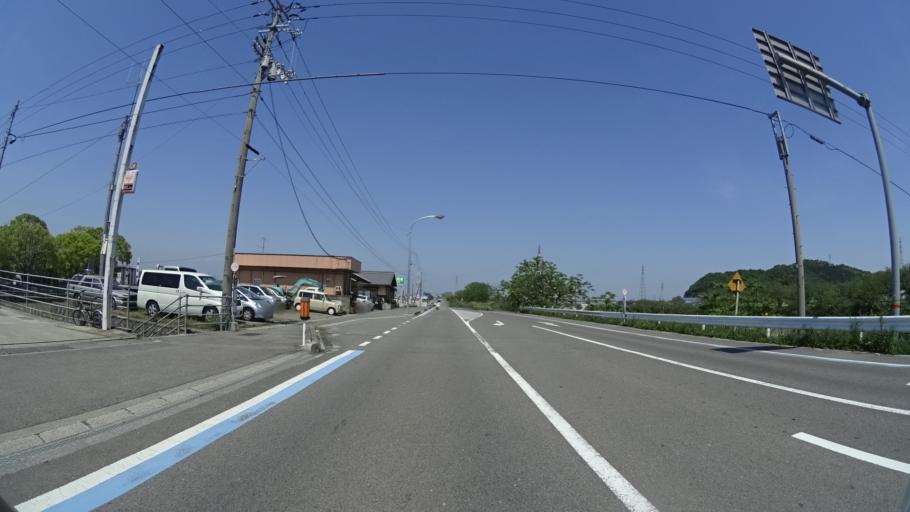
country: JP
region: Ehime
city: Hojo
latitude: 34.0327
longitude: 132.9689
